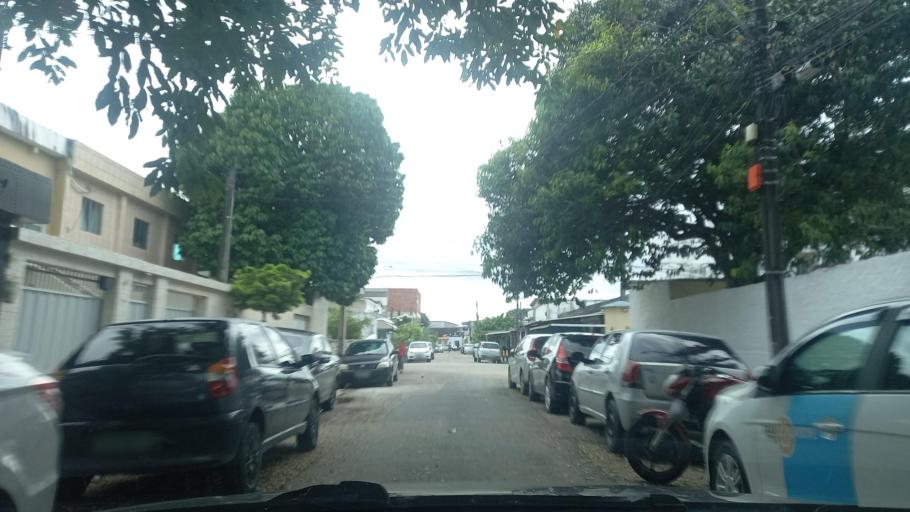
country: BR
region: Pernambuco
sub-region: Recife
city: Recife
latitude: -8.1088
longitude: -34.9214
